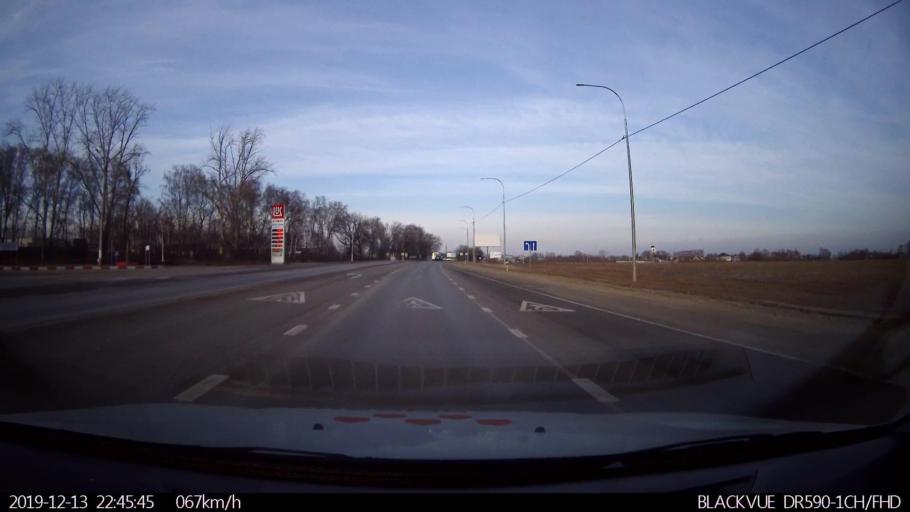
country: RU
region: Nizjnij Novgorod
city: Afonino
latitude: 56.2139
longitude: 44.1059
